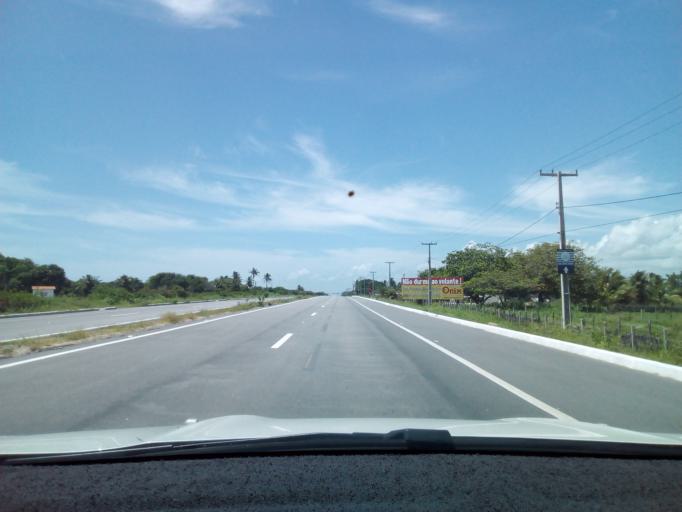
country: BR
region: Ceara
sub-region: Aracati
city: Aracati
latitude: -4.4401
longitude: -37.8238
